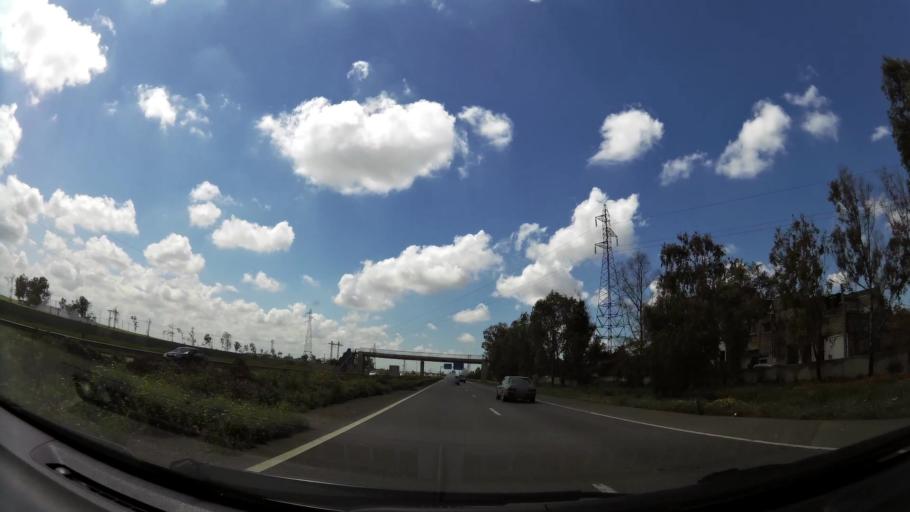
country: MA
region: Grand Casablanca
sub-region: Casablanca
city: Casablanca
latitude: 33.5138
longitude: -7.5990
